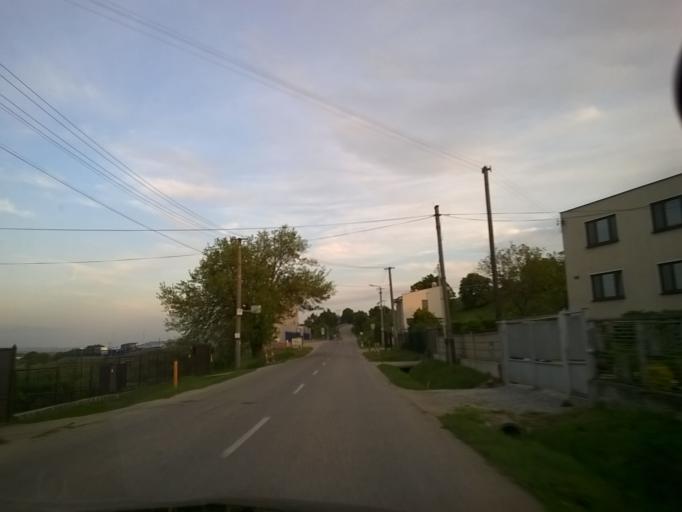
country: SK
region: Nitriansky
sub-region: Okres Nitra
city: Nitra
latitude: 48.3720
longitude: 18.1808
